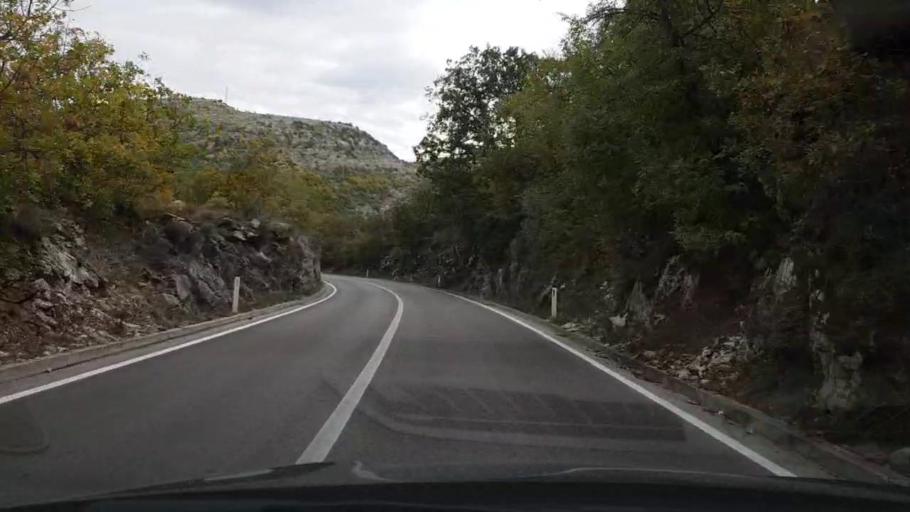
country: BA
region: Republika Srpska
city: Trebinje
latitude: 42.6817
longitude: 18.2979
